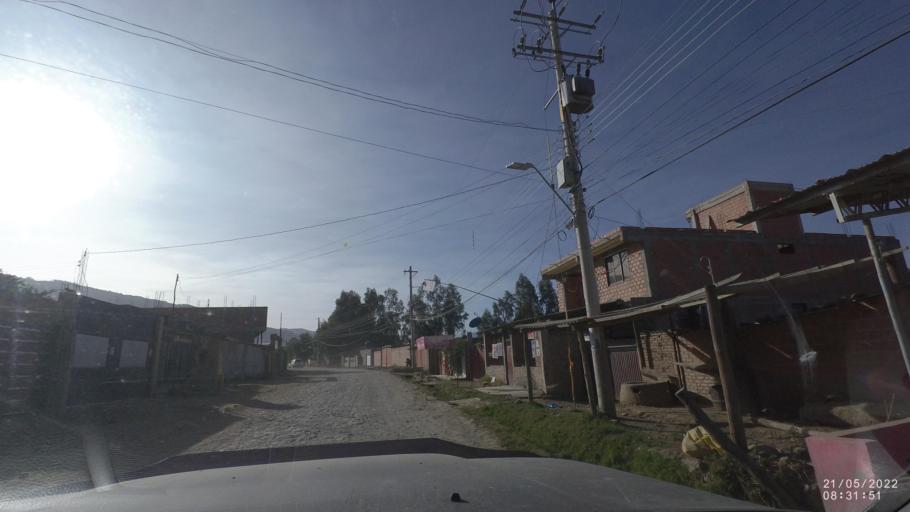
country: BO
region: Cochabamba
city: Cochabamba
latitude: -17.3851
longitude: -66.0554
